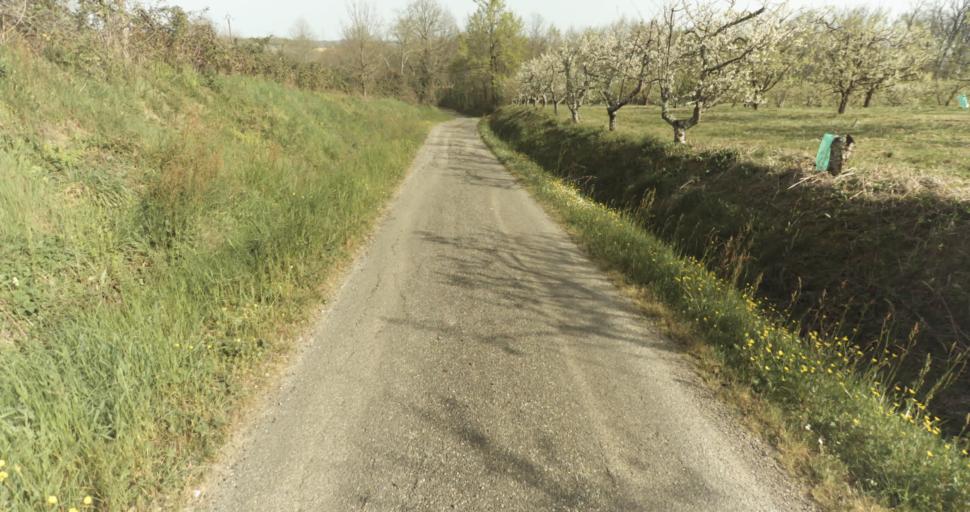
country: FR
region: Midi-Pyrenees
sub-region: Departement du Tarn-et-Garonne
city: Lafrancaise
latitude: 44.1491
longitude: 1.1716
